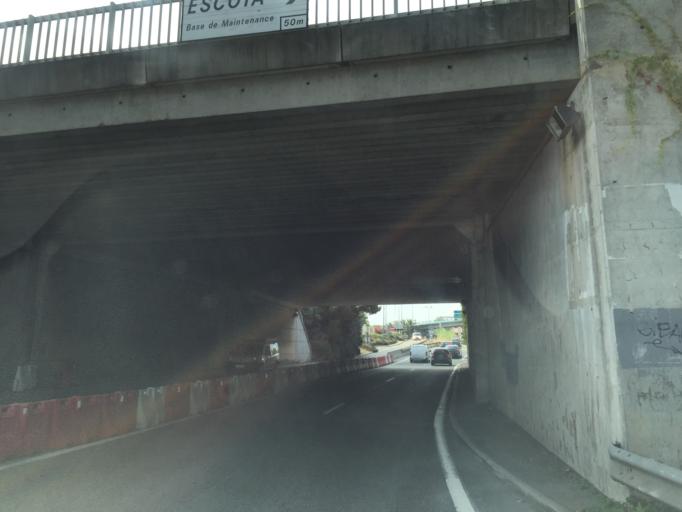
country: FR
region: Provence-Alpes-Cote d'Azur
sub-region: Departement des Alpes-Maritimes
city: Biot
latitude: 43.6038
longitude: 7.0831
